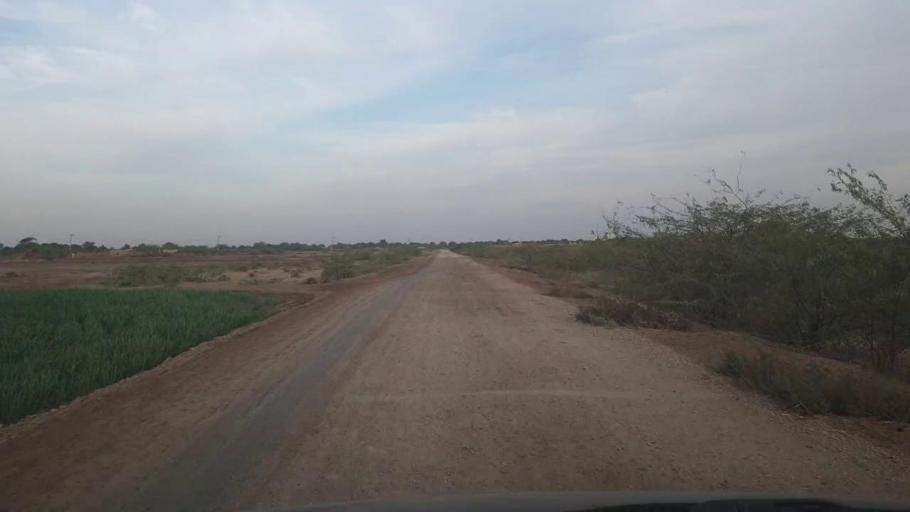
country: PK
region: Sindh
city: Kunri
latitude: 25.2385
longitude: 69.5513
